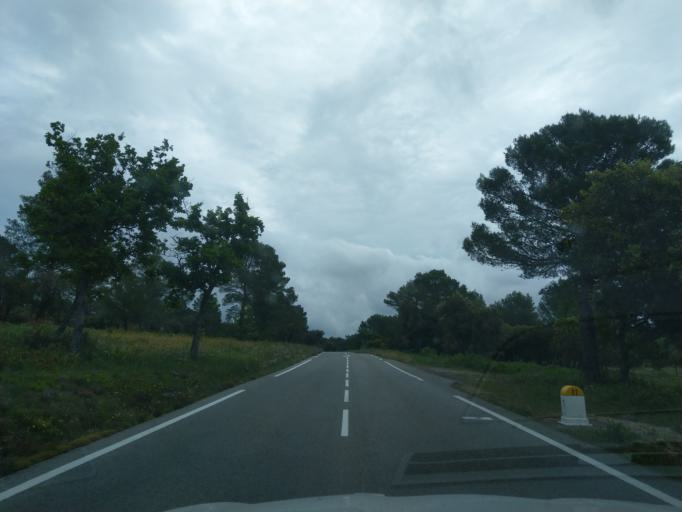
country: FR
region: Provence-Alpes-Cote d'Azur
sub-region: Departement du Var
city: Le Castellet
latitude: 43.2691
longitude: 5.7830
